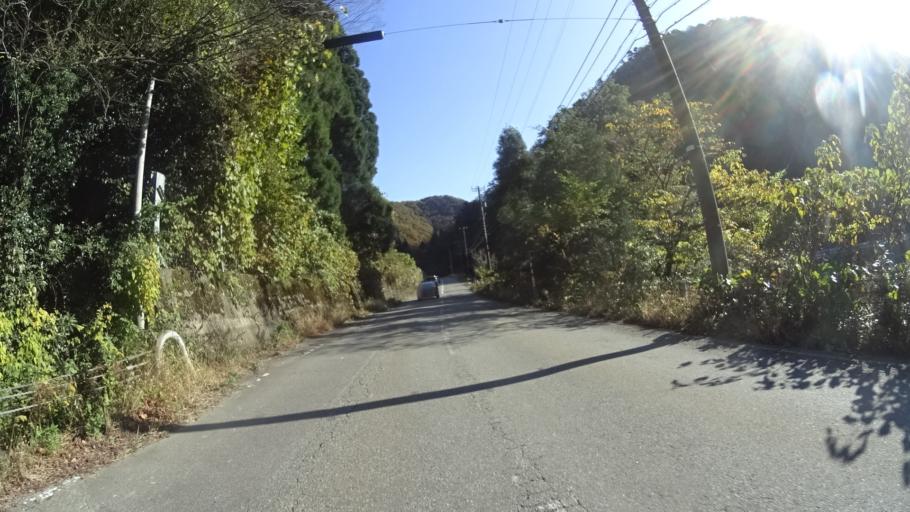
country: JP
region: Ishikawa
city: Tsurugi-asahimachi
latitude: 36.3734
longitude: 136.5631
